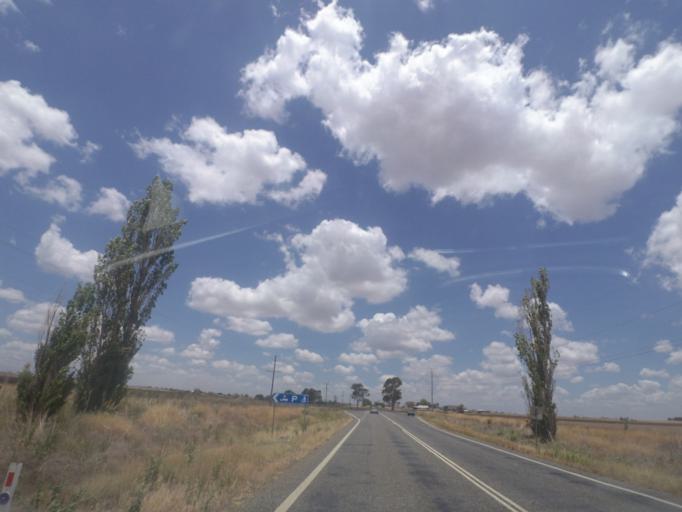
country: AU
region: Queensland
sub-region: Toowoomba
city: Top Camp
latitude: -27.9261
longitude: 151.9845
